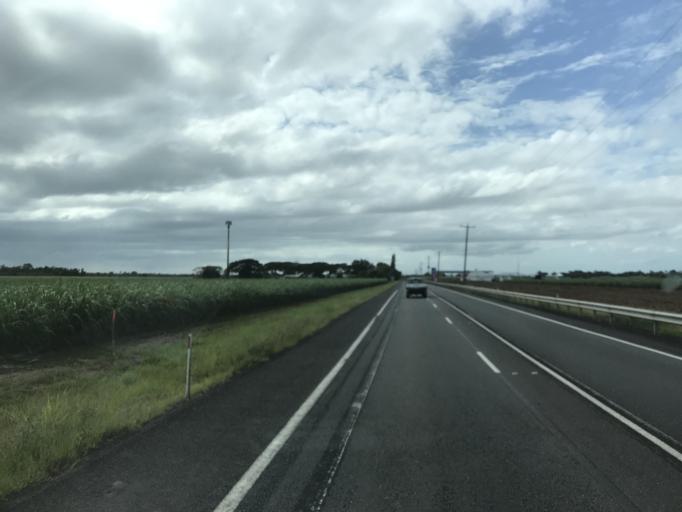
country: AU
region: Queensland
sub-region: Cassowary Coast
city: Innisfail
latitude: -17.5532
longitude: 146.0334
